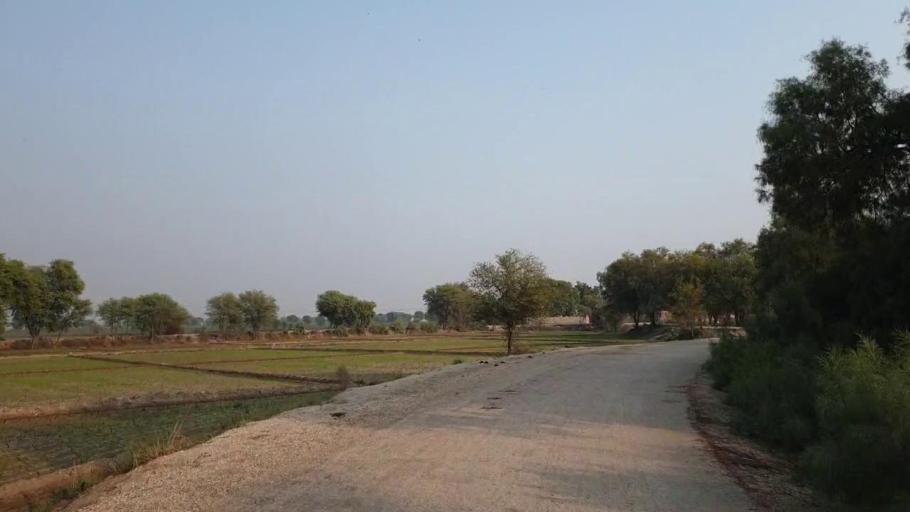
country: PK
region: Sindh
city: Bhan
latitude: 26.4995
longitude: 67.7641
